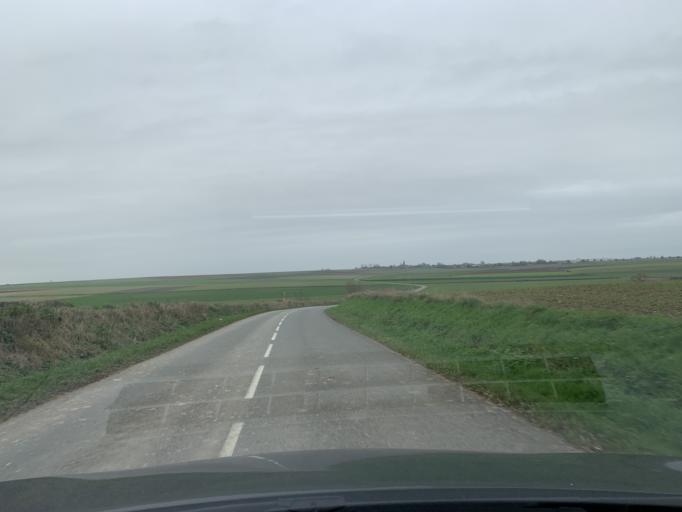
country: FR
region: Nord-Pas-de-Calais
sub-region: Departement du Pas-de-Calais
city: Oisy-le-Verger
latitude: 50.2444
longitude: 3.1347
